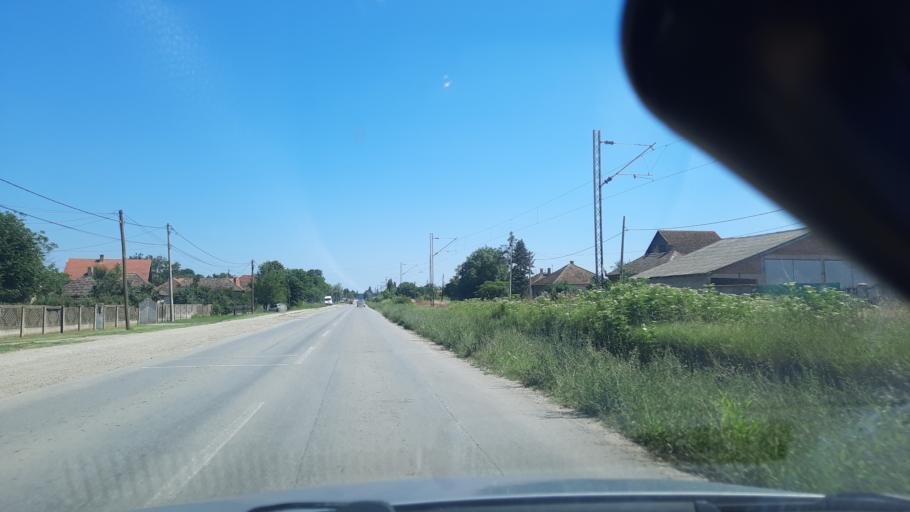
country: RS
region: Central Serbia
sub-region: Podunavski Okrug
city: Smederevo
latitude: 44.5954
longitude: 20.9922
